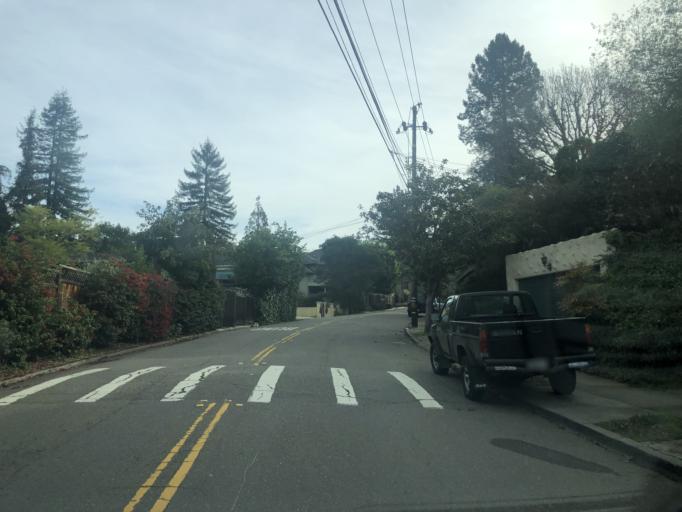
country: US
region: California
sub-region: Alameda County
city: Piedmont
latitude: 37.8536
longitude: -122.2428
